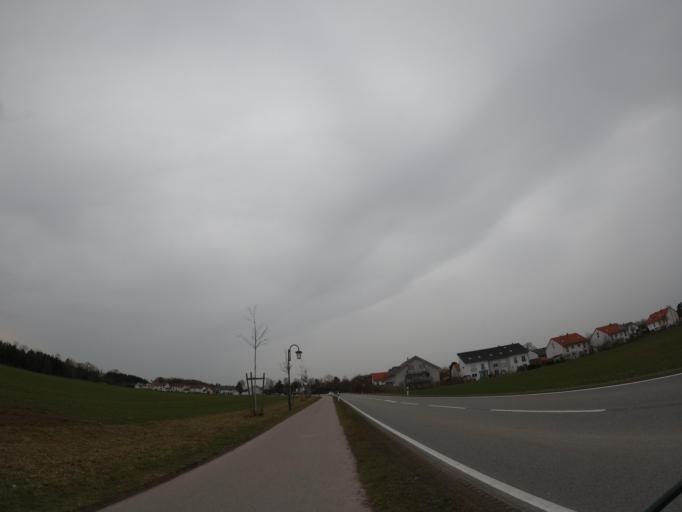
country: DE
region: Bavaria
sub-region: Upper Bavaria
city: Putzbrunn
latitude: 48.0762
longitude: 11.7053
